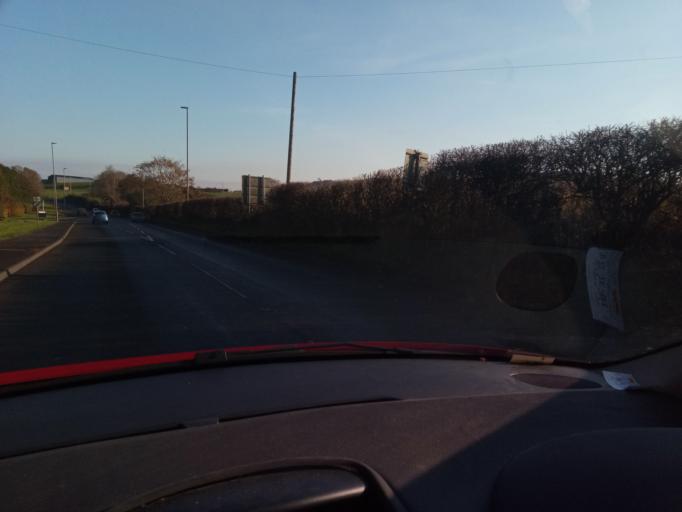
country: GB
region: Scotland
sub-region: The Scottish Borders
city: Hawick
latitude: 55.4355
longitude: -2.7516
